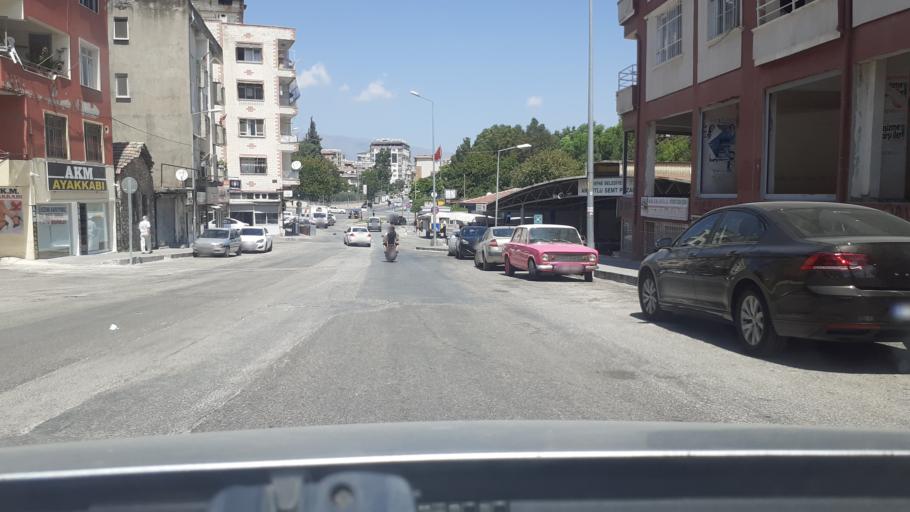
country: TR
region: Hatay
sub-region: Antakya Ilcesi
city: Antakya
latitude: 36.1985
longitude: 36.1544
